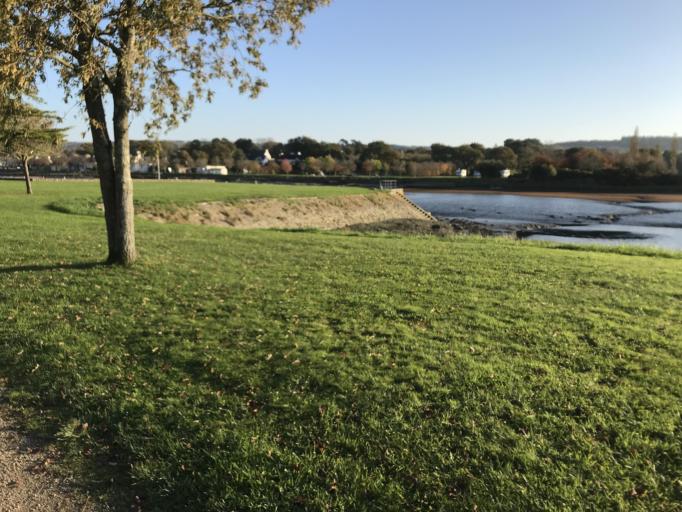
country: FR
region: Brittany
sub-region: Departement du Finistere
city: Le Faou
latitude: 48.2970
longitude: -4.1877
